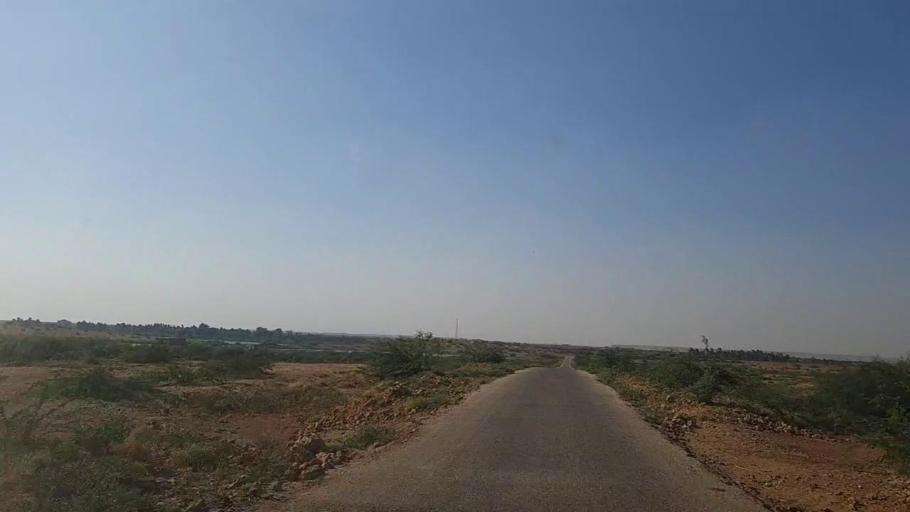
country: PK
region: Sindh
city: Daro Mehar
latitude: 24.9982
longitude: 68.1284
